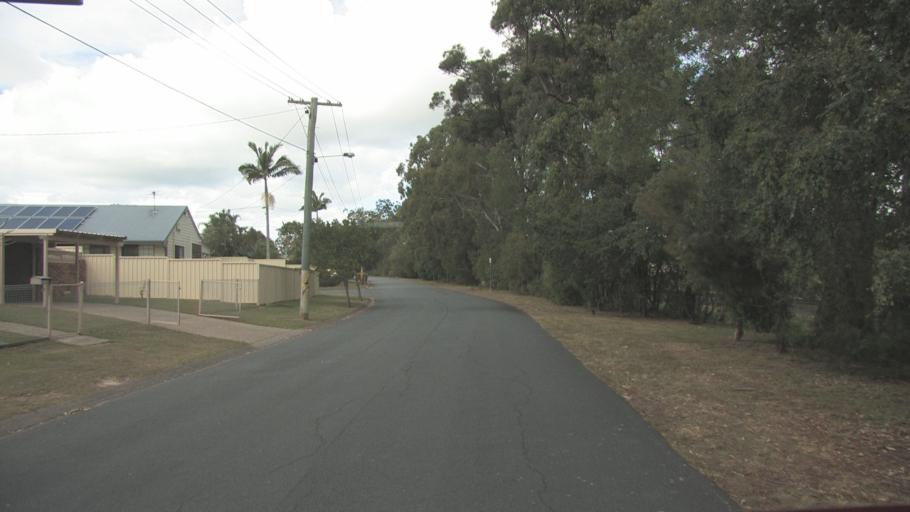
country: AU
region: Queensland
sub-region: Brisbane
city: Forest Lake
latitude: -27.6640
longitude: 153.0191
